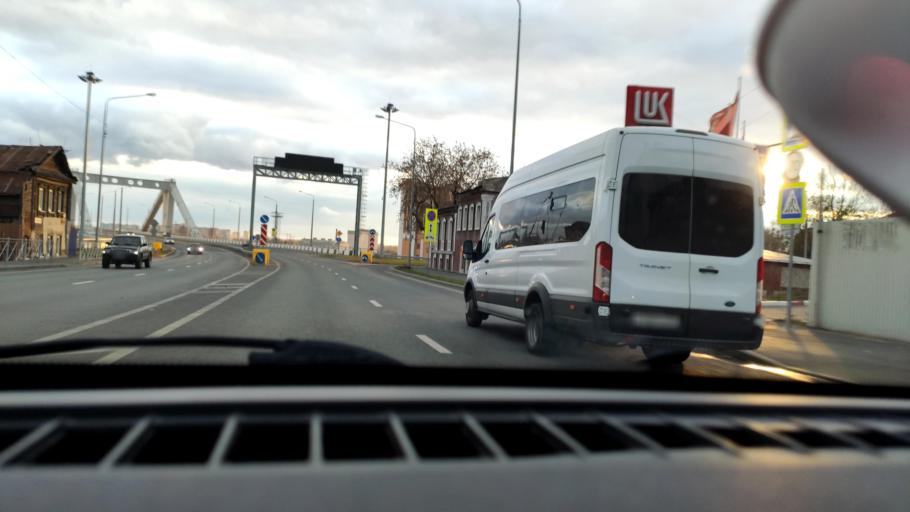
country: RU
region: Samara
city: Rozhdestveno
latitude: 53.1794
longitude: 50.0861
